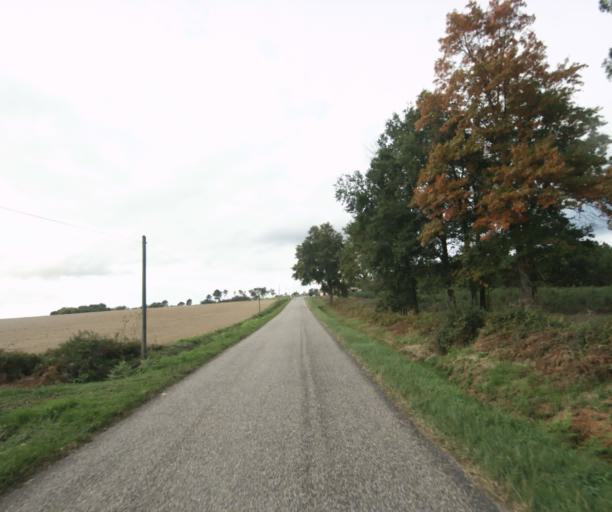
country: FR
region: Midi-Pyrenees
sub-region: Departement du Gers
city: Eauze
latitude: 43.9110
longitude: 0.0988
